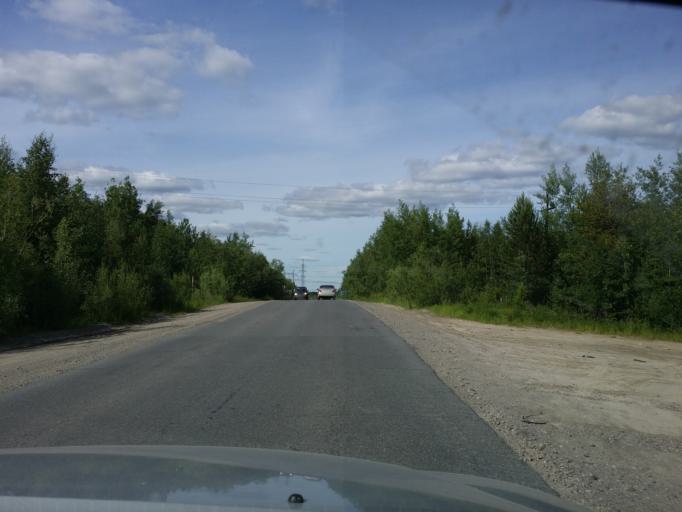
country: RU
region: Khanty-Mansiyskiy Avtonomnyy Okrug
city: Nizhnevartovsk
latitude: 60.9953
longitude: 76.5636
